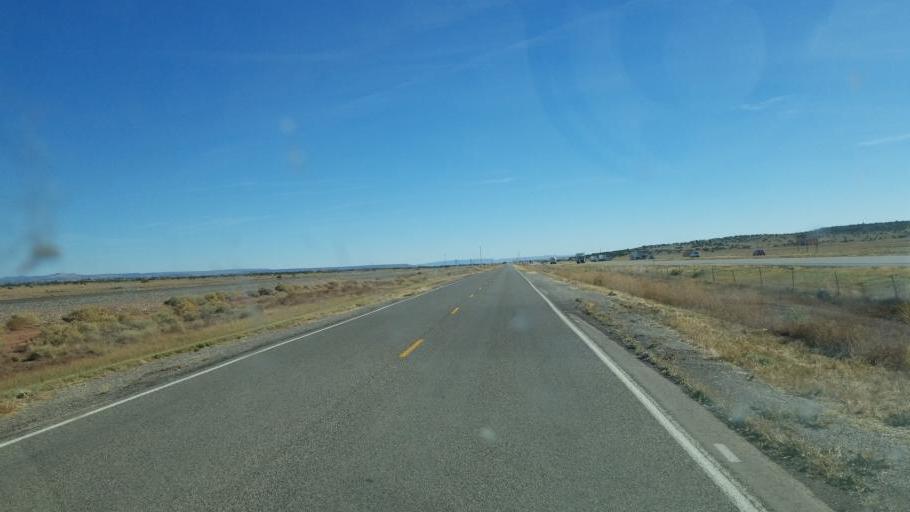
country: US
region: New Mexico
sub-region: Cibola County
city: Milan
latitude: 35.3340
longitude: -108.0024
